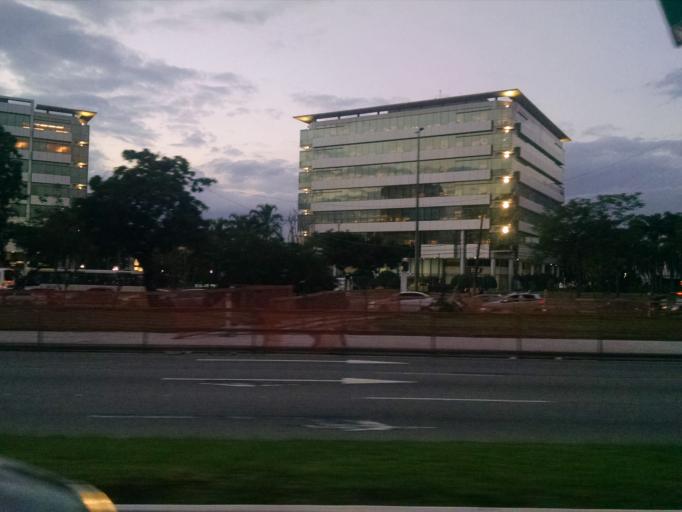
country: BR
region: Rio de Janeiro
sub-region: Rio De Janeiro
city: Rio de Janeiro
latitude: -23.0005
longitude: -43.3459
